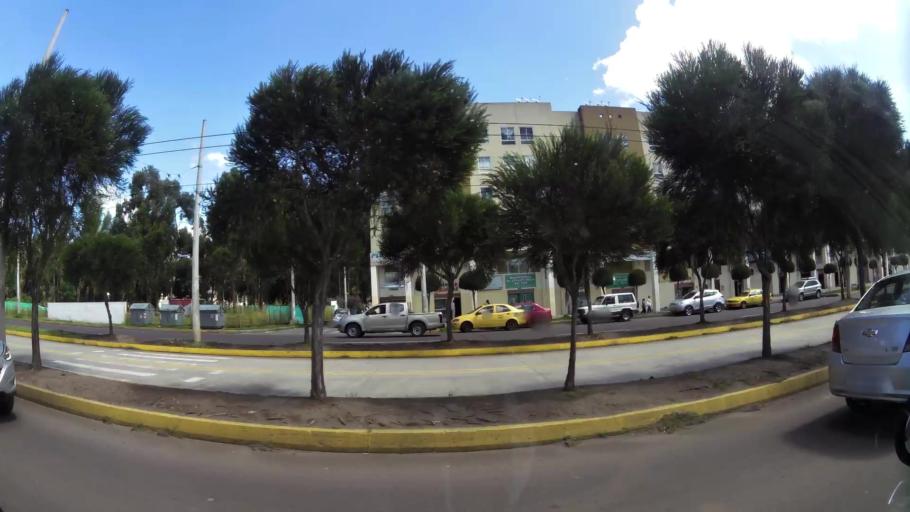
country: EC
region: Pichincha
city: Quito
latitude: -0.2956
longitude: -78.5490
